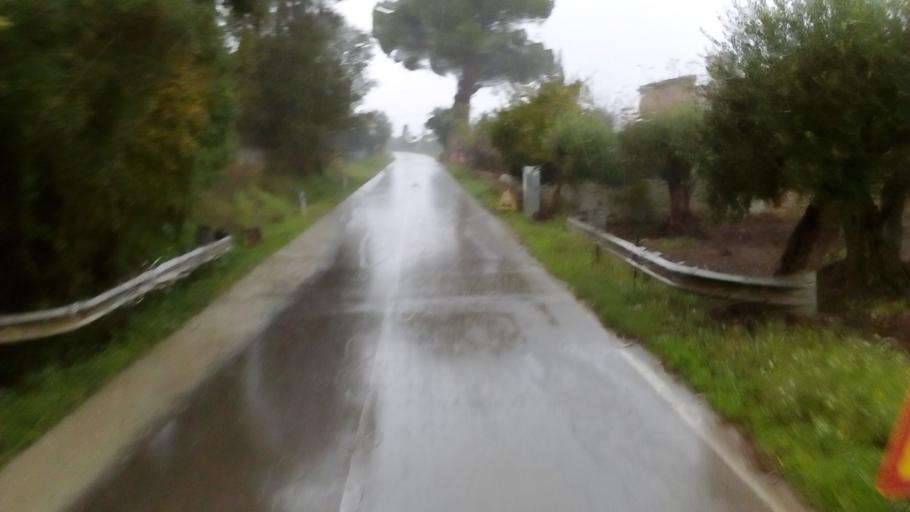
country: IT
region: Sicily
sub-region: Enna
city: Pietraperzia
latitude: 37.4207
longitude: 14.1662
